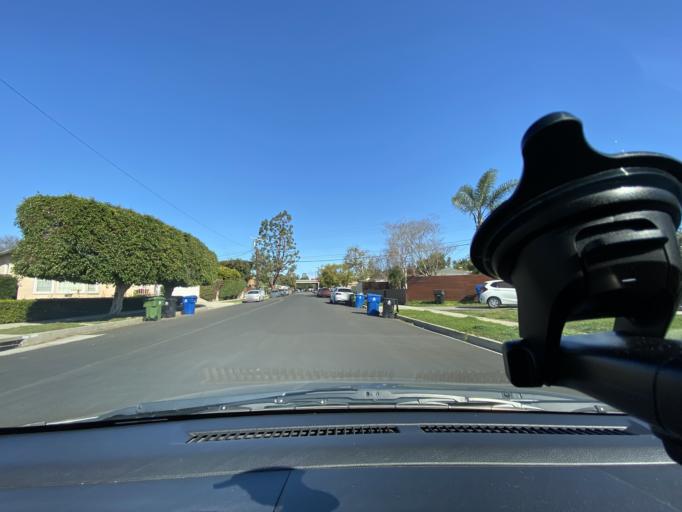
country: US
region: California
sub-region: Los Angeles County
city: Century City
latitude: 34.0297
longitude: -118.4249
